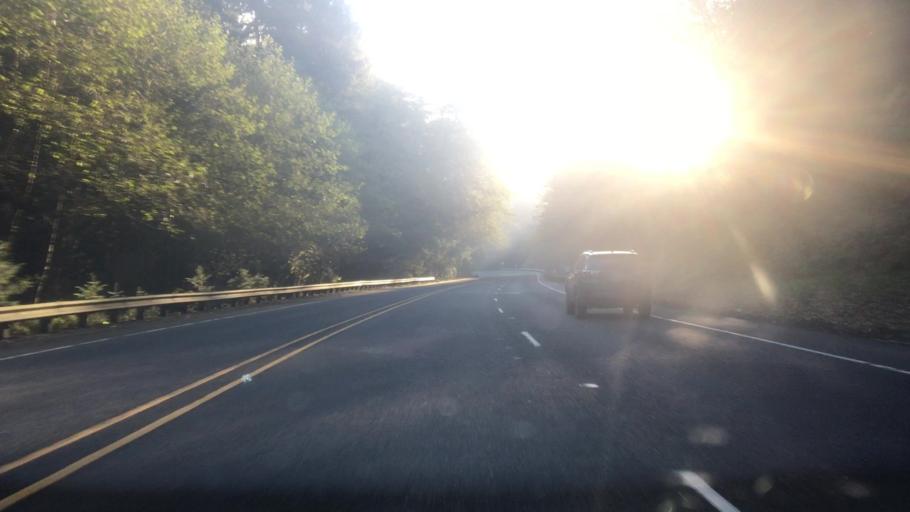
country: US
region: Oregon
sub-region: Clatsop County
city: Cannon Beach
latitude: 45.9224
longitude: -123.9337
